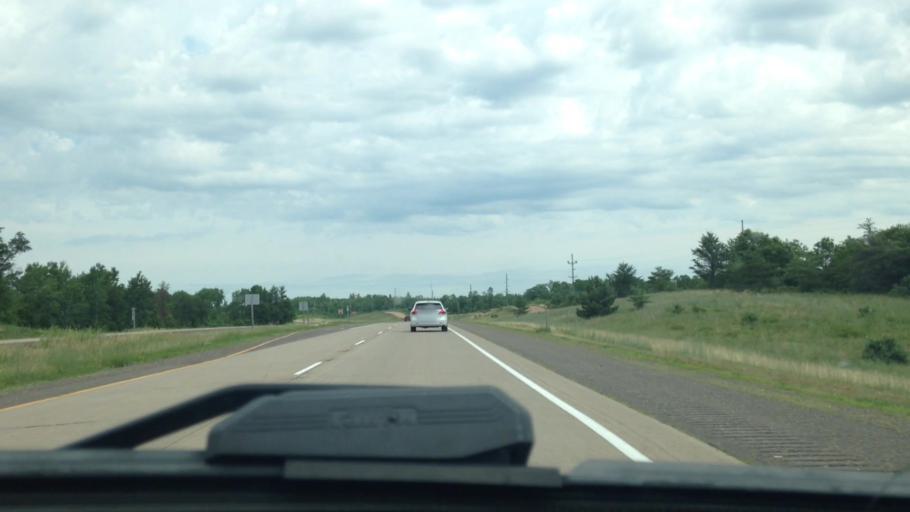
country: US
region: Wisconsin
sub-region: Douglas County
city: Lake Nebagamon
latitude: 46.2078
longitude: -91.7980
